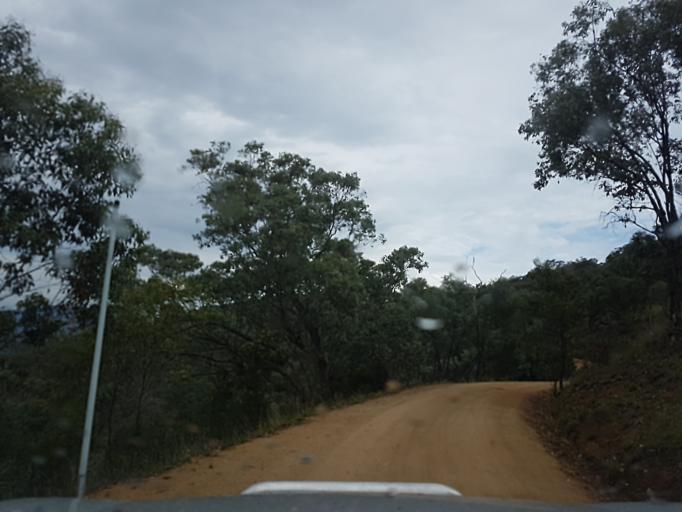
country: AU
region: New South Wales
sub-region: Snowy River
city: Jindabyne
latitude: -36.9478
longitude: 148.3484
